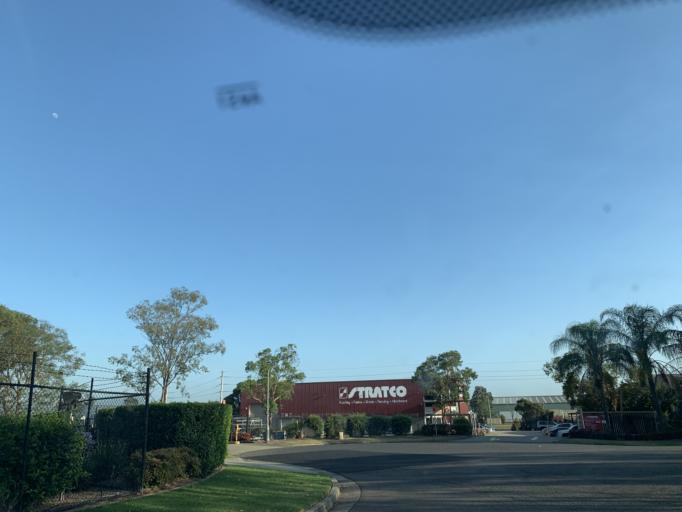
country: AU
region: New South Wales
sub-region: Blacktown
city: Doonside
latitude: -33.7943
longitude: 150.8728
